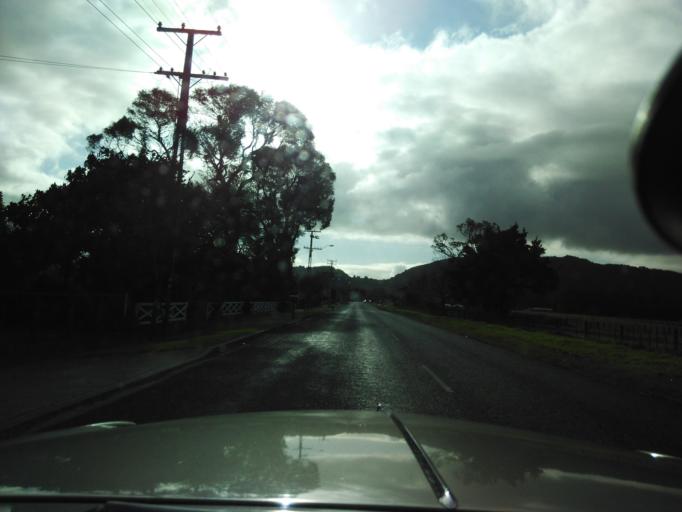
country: NZ
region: Auckland
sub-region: Auckland
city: Red Hill
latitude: -36.9998
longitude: 175.0396
